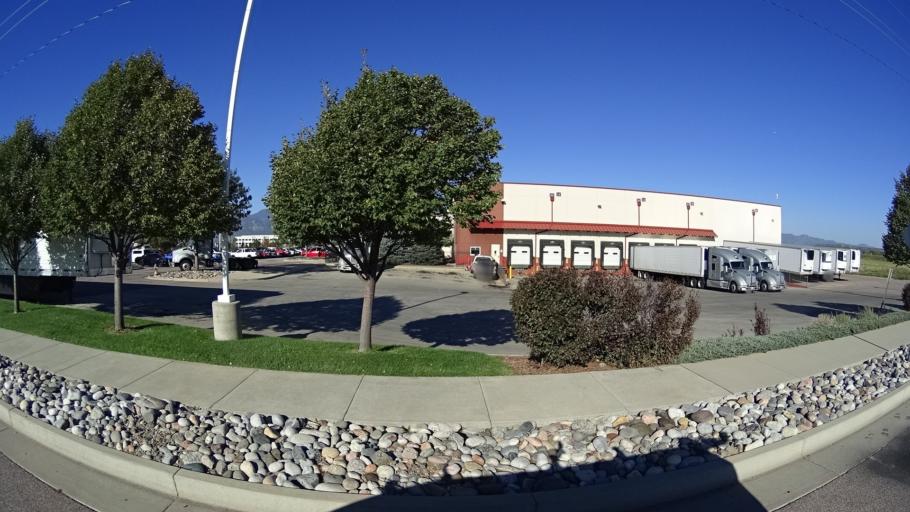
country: US
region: Colorado
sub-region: El Paso County
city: Cimarron Hills
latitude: 38.8191
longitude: -104.7225
